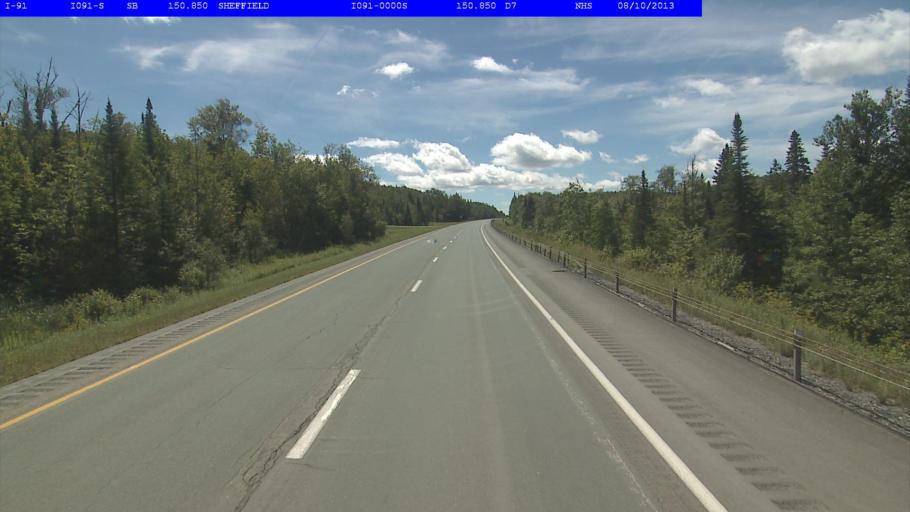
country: US
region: Vermont
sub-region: Caledonia County
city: Lyndonville
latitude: 44.6769
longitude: -72.1329
